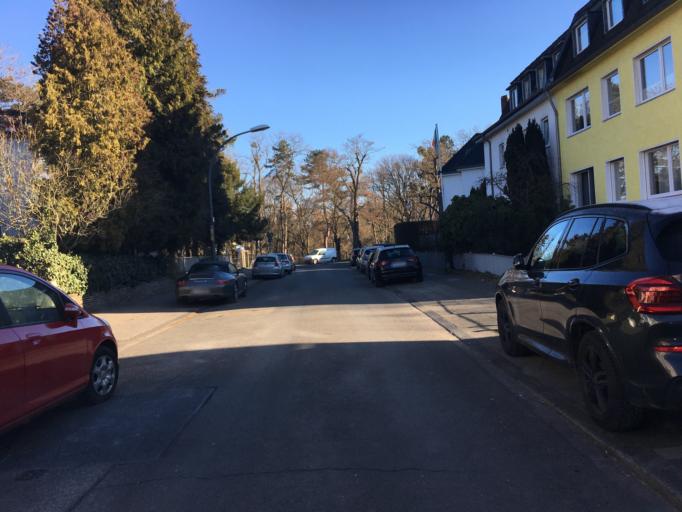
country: DE
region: North Rhine-Westphalia
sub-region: Regierungsbezirk Koln
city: Neustadt/Sued
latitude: 50.9068
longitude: 6.9214
